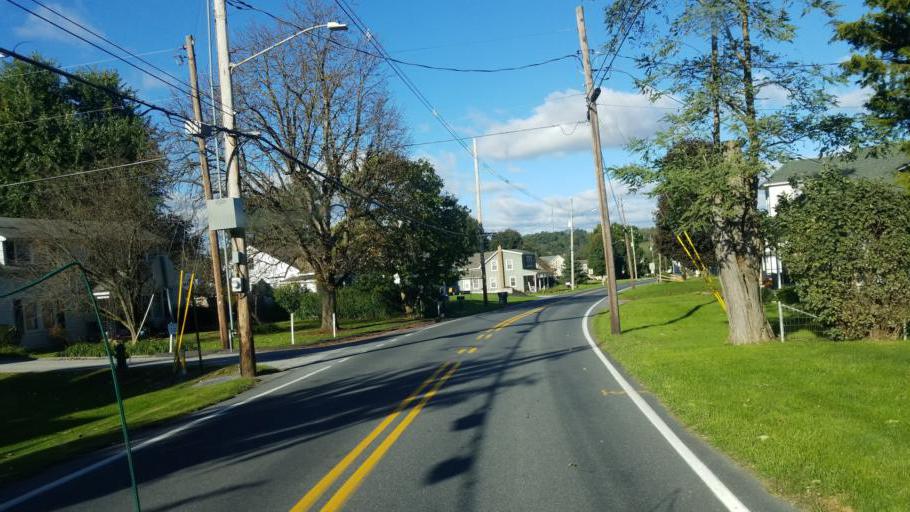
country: US
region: Pennsylvania
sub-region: Franklin County
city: Mont Alto
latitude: 39.8423
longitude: -77.5527
